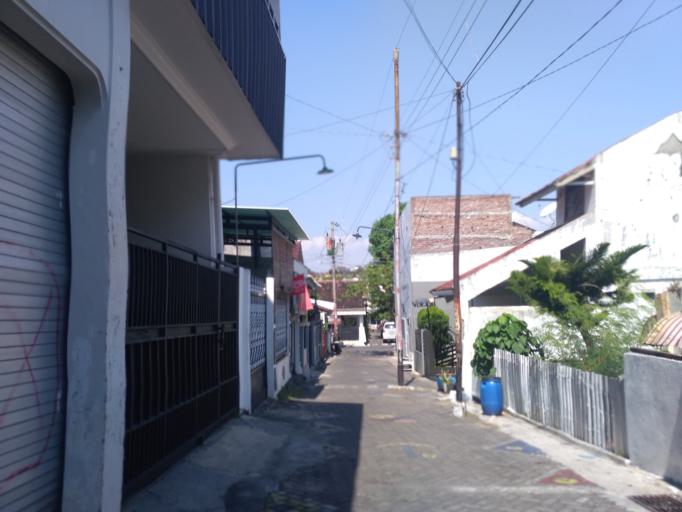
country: ID
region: Central Java
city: Semarang
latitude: -6.9986
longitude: 110.4305
